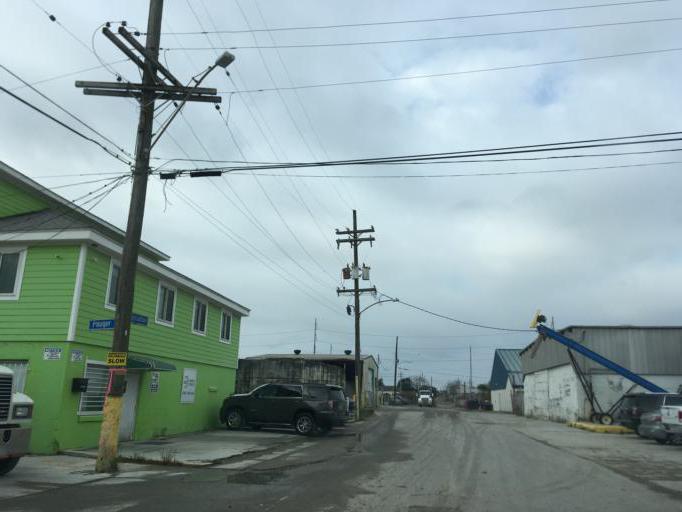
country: US
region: Louisiana
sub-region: Orleans Parish
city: New Orleans
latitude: 29.9876
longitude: -90.0619
